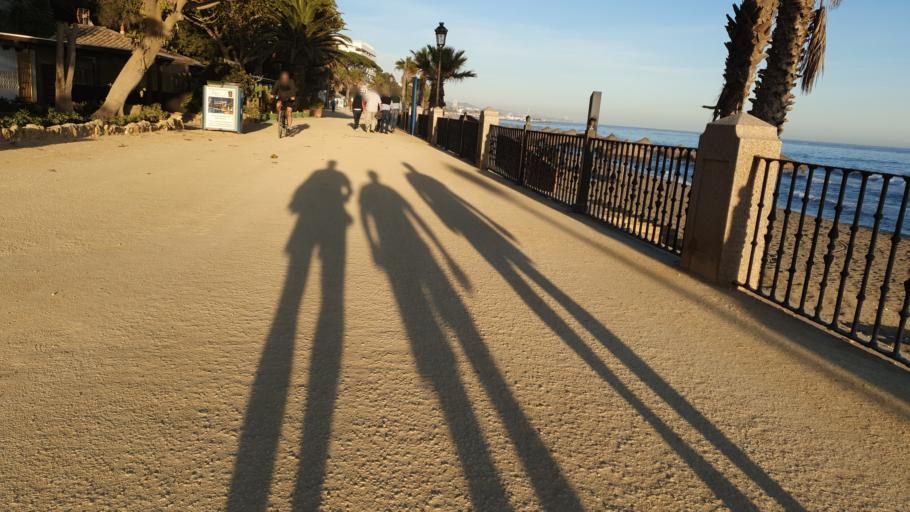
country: ES
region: Andalusia
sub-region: Provincia de Malaga
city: Marbella
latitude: 36.5062
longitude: -4.9078
